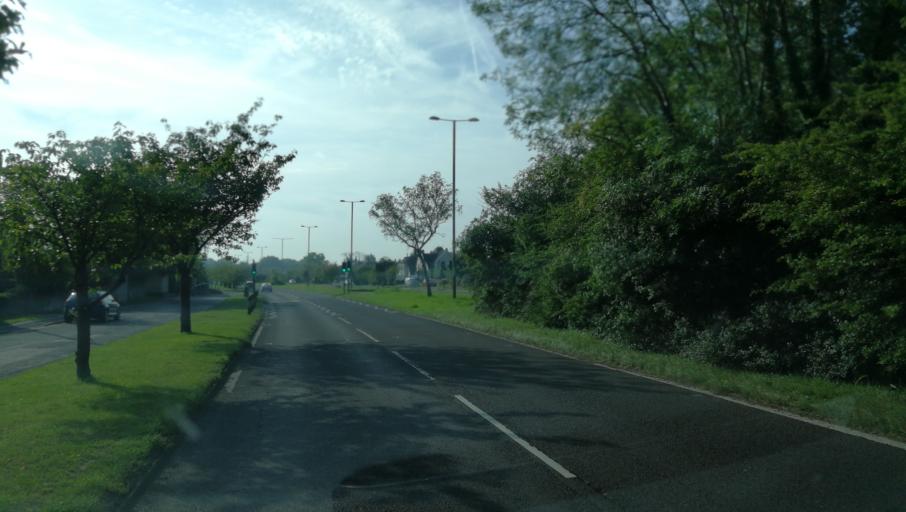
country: GB
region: England
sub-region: Oxfordshire
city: Yarnton
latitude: 51.8122
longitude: -1.3106
